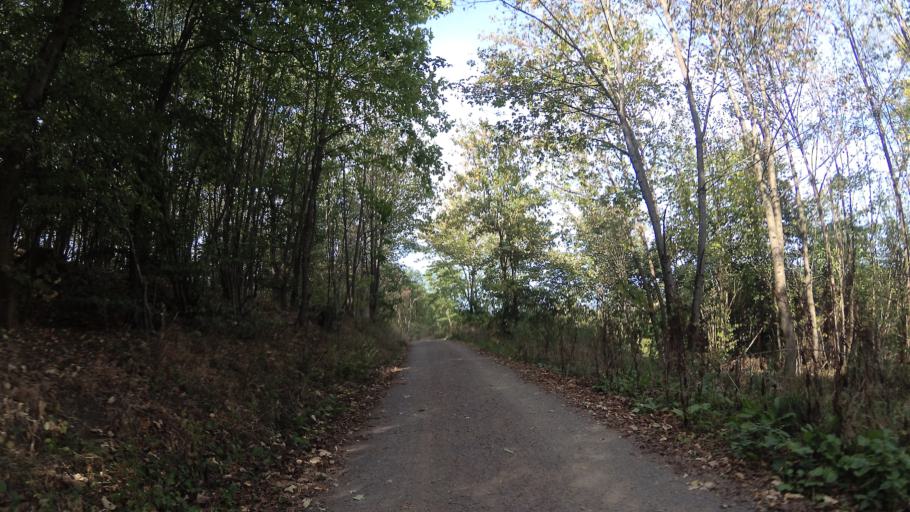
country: DE
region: Saarland
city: Sankt Wendel
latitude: 49.4753
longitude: 7.2028
